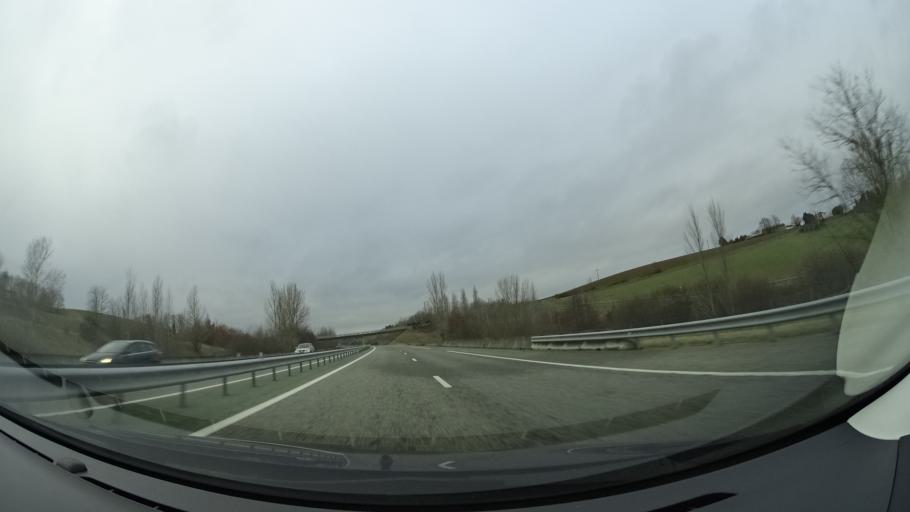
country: FR
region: Midi-Pyrenees
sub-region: Departement de l'Ariege
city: Mazeres
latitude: 43.2893
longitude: 1.6724
